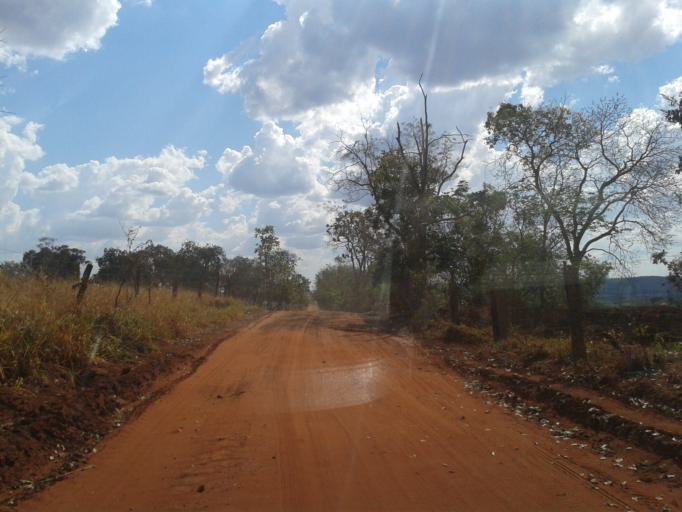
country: BR
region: Minas Gerais
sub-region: Santa Vitoria
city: Santa Vitoria
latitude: -19.1986
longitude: -49.9093
